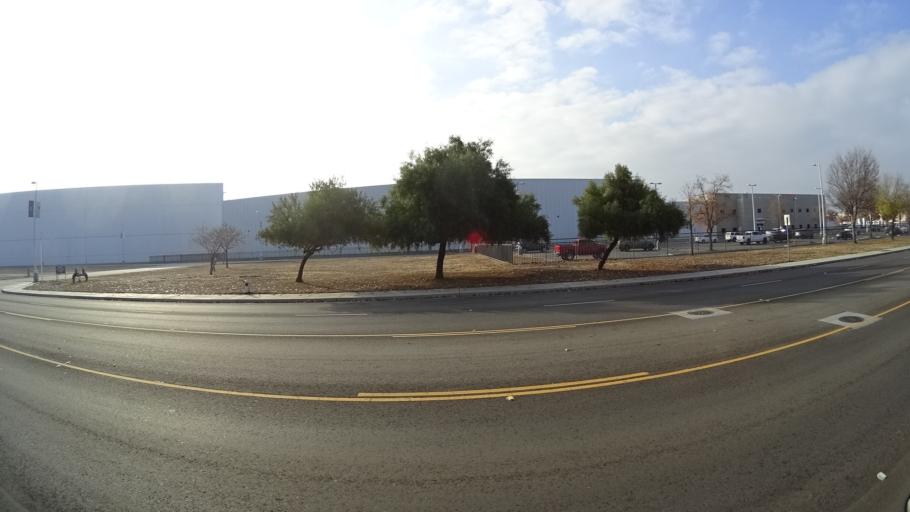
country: US
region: California
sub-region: Kern County
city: Greenacres
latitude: 35.3132
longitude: -119.0870
